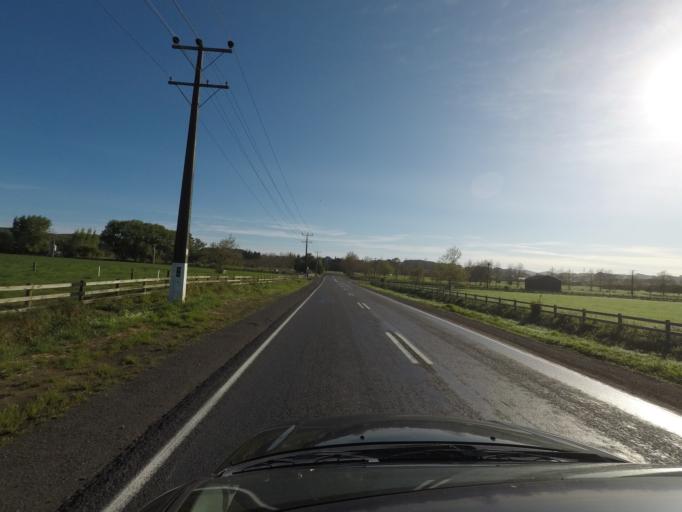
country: NZ
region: Auckland
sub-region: Auckland
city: Red Hill
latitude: -37.0055
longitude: 174.9553
